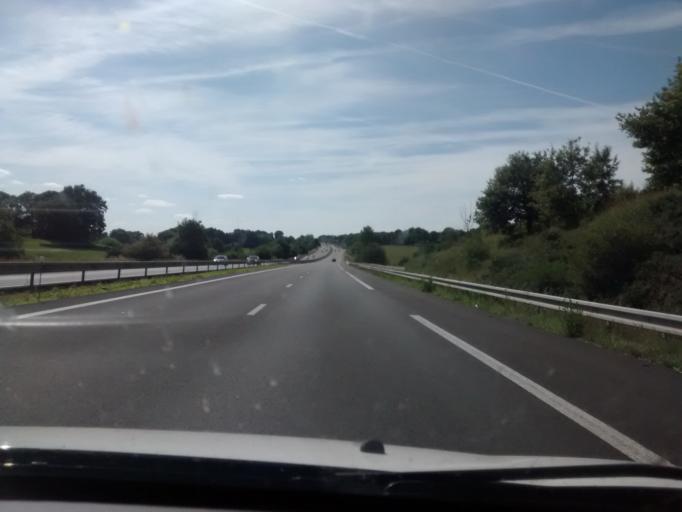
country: FR
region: Pays de la Loire
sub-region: Departement de la Mayenne
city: Vaiges
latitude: 48.0531
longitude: -0.4707
